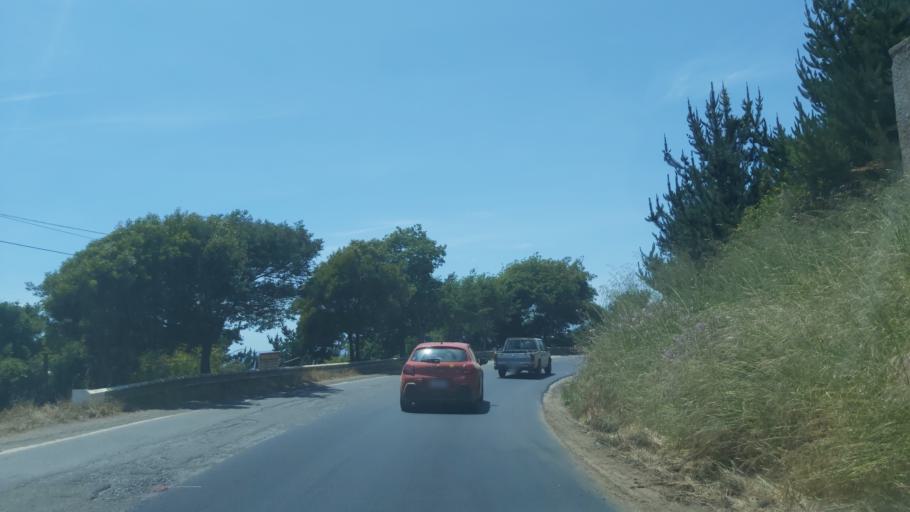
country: CL
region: Maule
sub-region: Provincia de Cauquenes
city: Cauquenes
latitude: -35.8239
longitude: -72.6036
